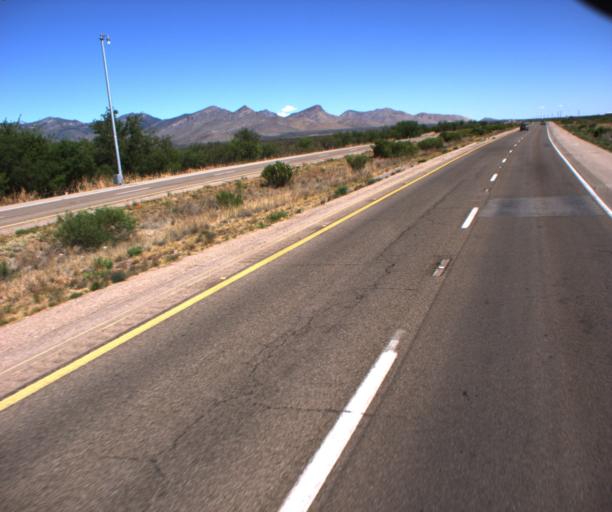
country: US
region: Arizona
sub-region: Cochise County
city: Huachuca City
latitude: 31.7214
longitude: -110.3502
